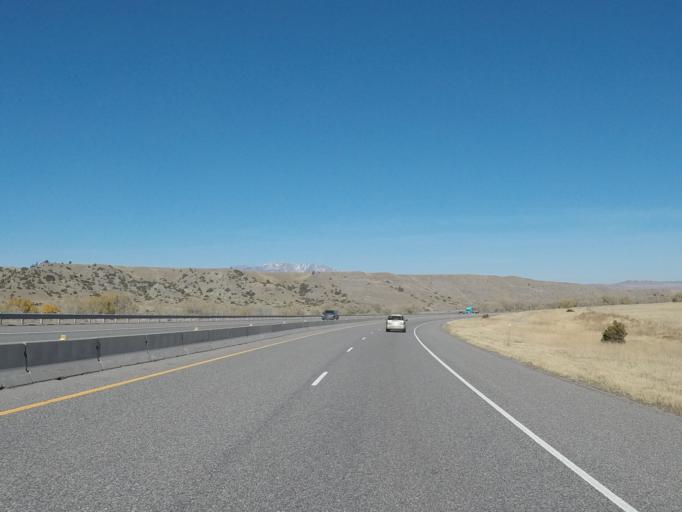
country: US
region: Montana
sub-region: Park County
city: Livingston
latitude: 45.7125
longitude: -110.2633
